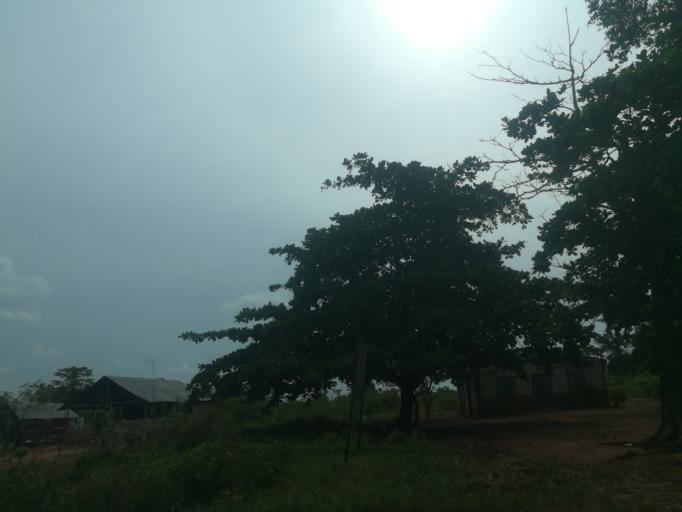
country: NG
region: Ogun
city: Ayetoro
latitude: 7.2831
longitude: 3.0894
